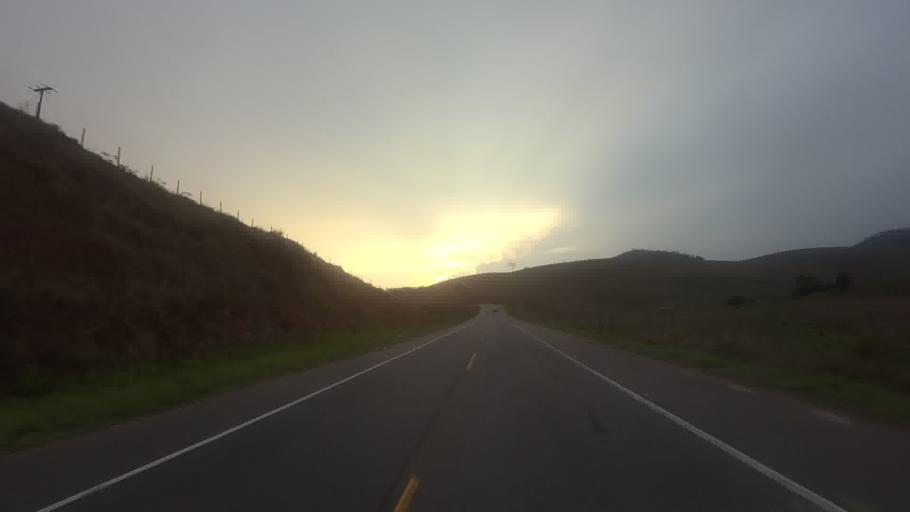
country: BR
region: Rio de Janeiro
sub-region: Carmo
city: Carmo
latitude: -21.7596
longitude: -42.4914
